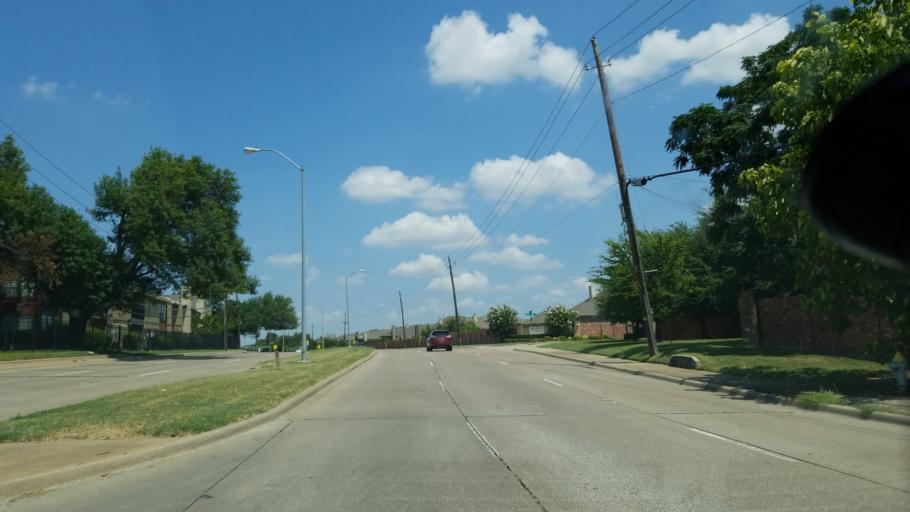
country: US
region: Texas
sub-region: Dallas County
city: Richardson
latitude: 32.9127
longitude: -96.7180
